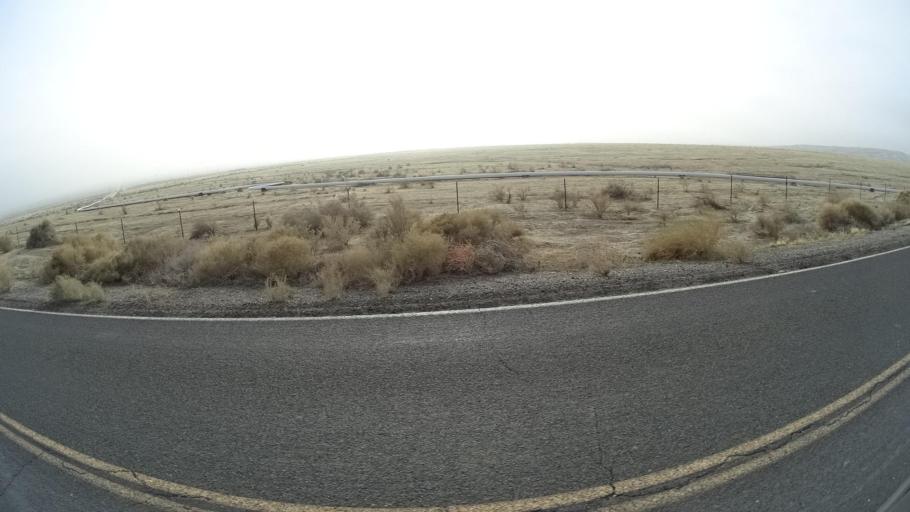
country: US
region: California
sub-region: Kern County
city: Ford City
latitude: 35.2377
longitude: -119.4478
